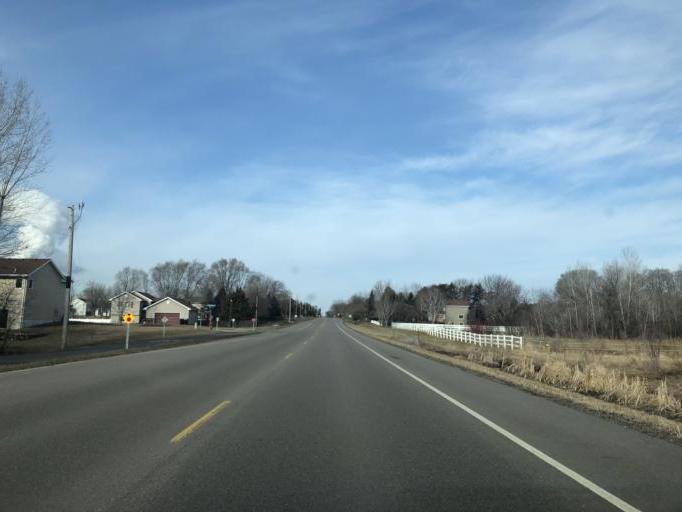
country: US
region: Minnesota
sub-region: Sherburne County
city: Becker
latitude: 45.3937
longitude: -93.8594
